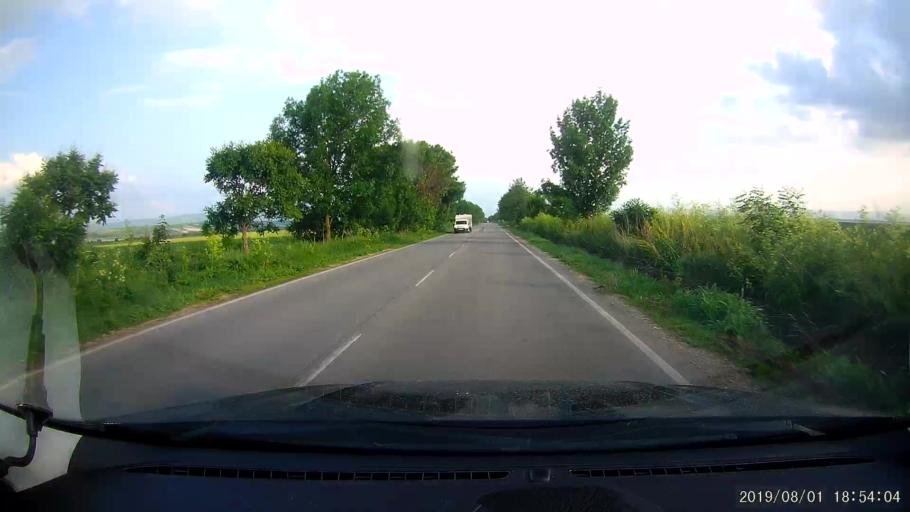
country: BG
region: Shumen
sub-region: Obshtina Shumen
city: Shumen
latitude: 43.2077
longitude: 26.9993
